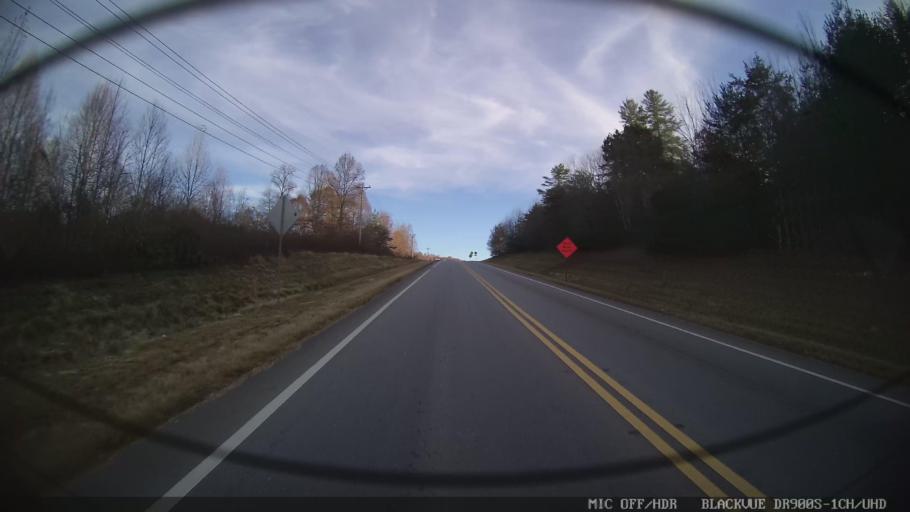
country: US
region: Georgia
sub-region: Union County
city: Blairsville
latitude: 34.8808
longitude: -83.9496
